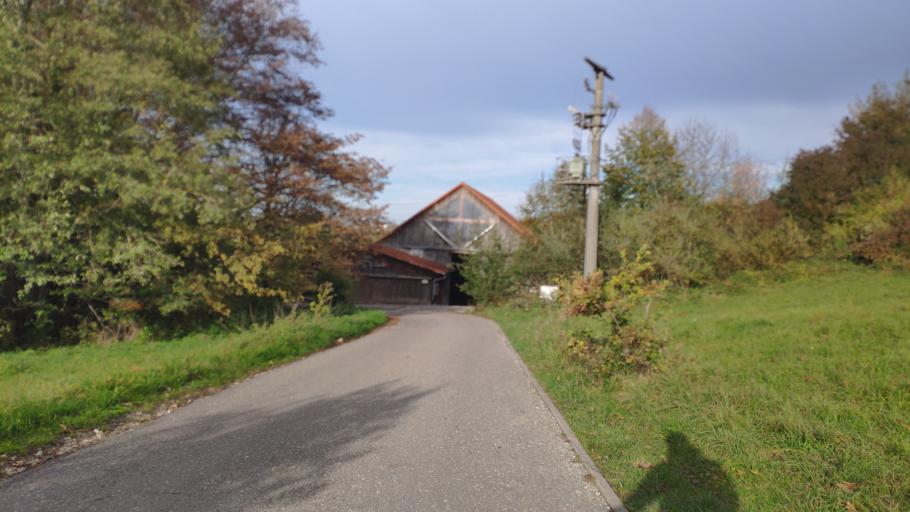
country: DE
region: Baden-Wuerttemberg
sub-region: Tuebingen Region
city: Erbach
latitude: 48.3814
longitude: 9.9197
